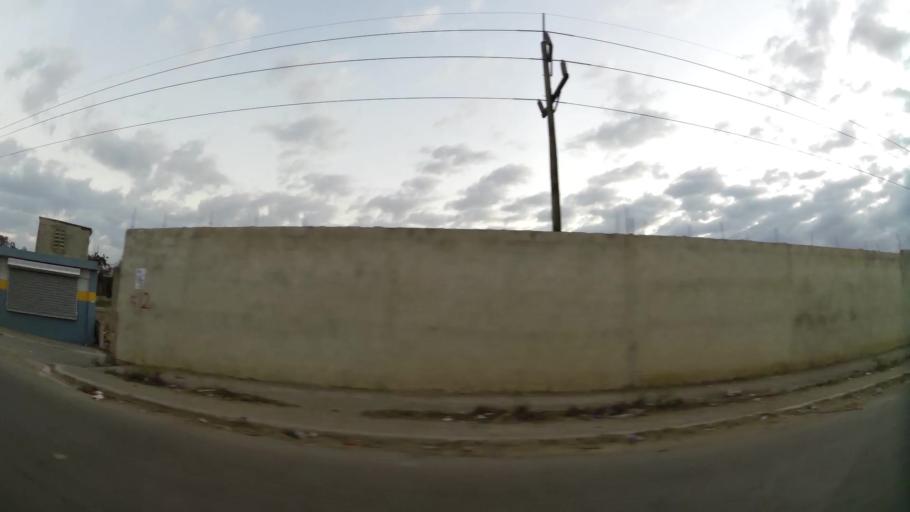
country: DO
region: Nacional
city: La Agustina
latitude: 18.5542
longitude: -69.9467
